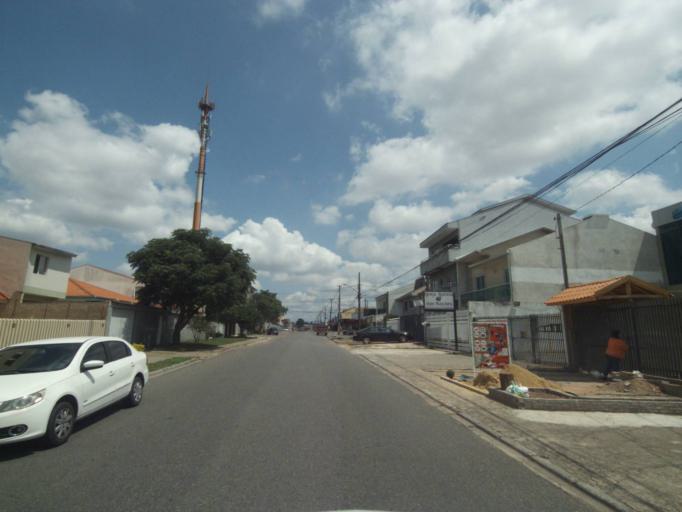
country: BR
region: Parana
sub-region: Sao Jose Dos Pinhais
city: Sao Jose dos Pinhais
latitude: -25.5421
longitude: -49.2585
